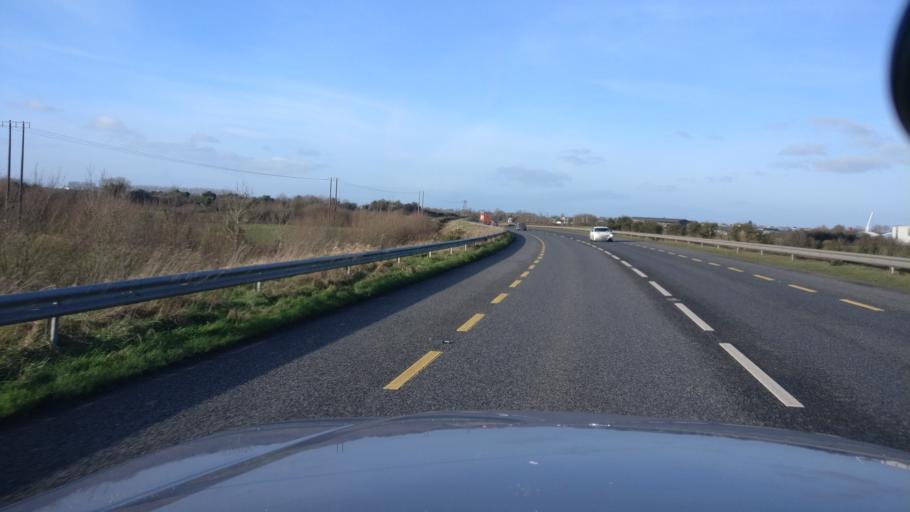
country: IE
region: Leinster
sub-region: Uibh Fhaili
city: Tullamore
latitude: 53.2701
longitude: -7.4634
